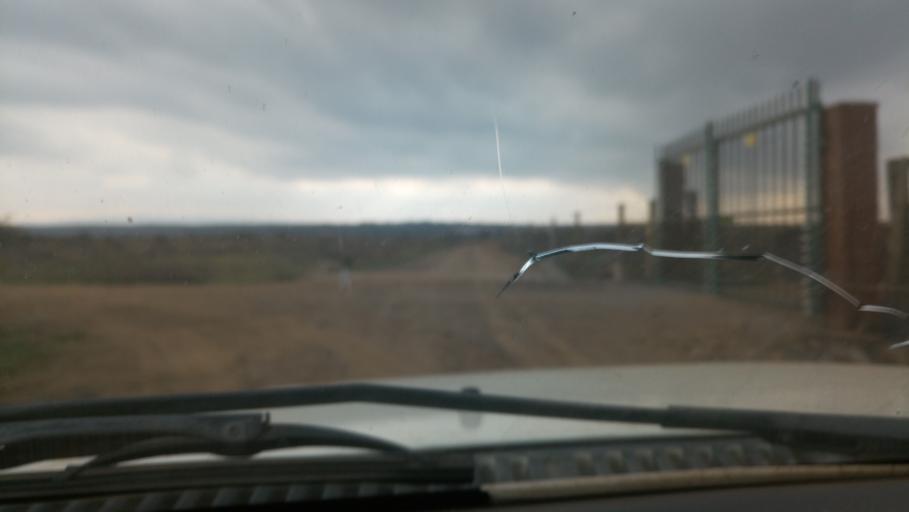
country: KE
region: Nairobi Area
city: Nairobi
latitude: -1.3331
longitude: 36.8238
